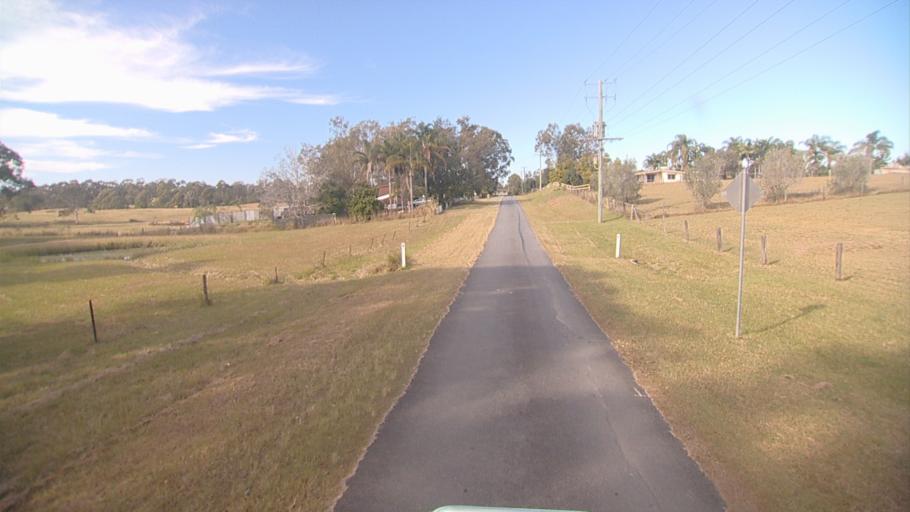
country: AU
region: Queensland
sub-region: Logan
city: Chambers Flat
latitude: -27.7471
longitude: 153.0612
